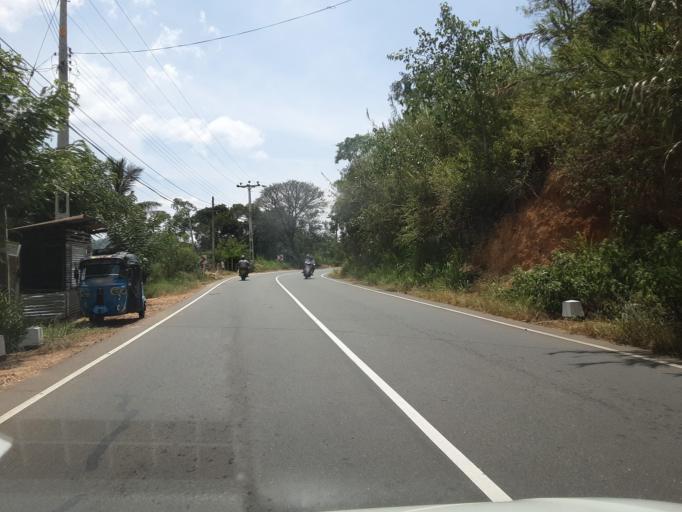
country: LK
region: Central
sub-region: Nuwara Eliya District
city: Nuwara Eliya
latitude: 6.9343
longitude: 80.9065
